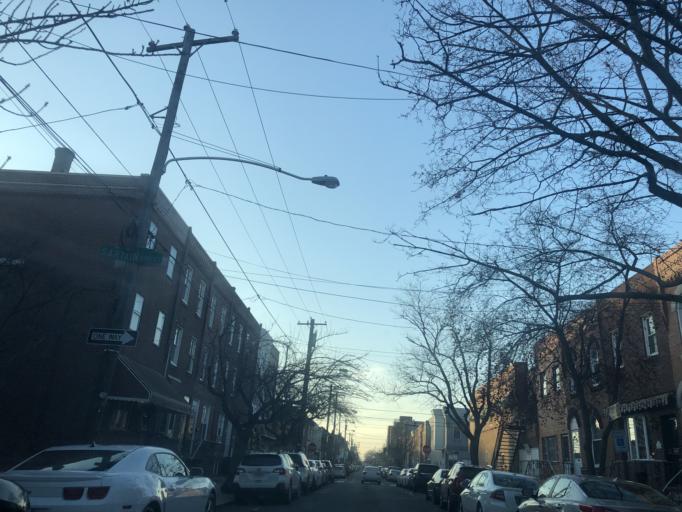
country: US
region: Pennsylvania
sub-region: Philadelphia County
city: Philadelphia
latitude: 39.9201
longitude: -75.1660
